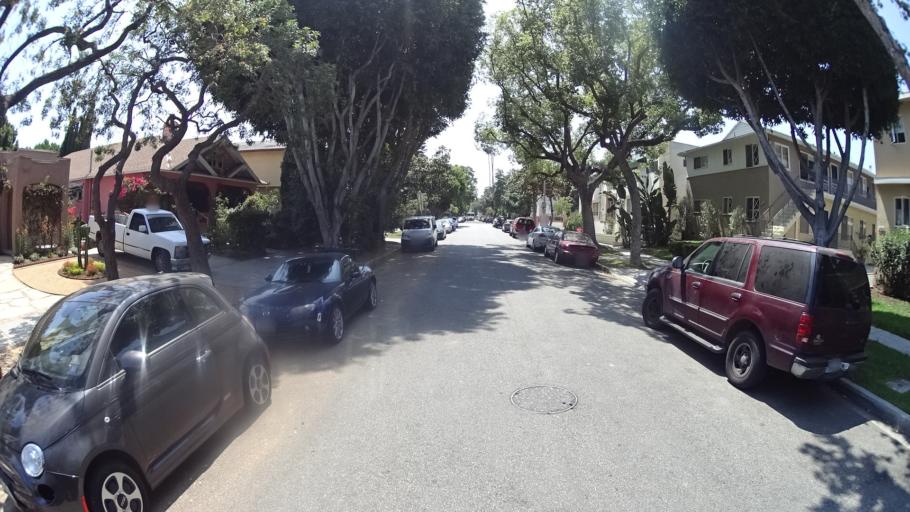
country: US
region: California
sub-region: Los Angeles County
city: West Hollywood
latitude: 34.0934
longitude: -118.3559
